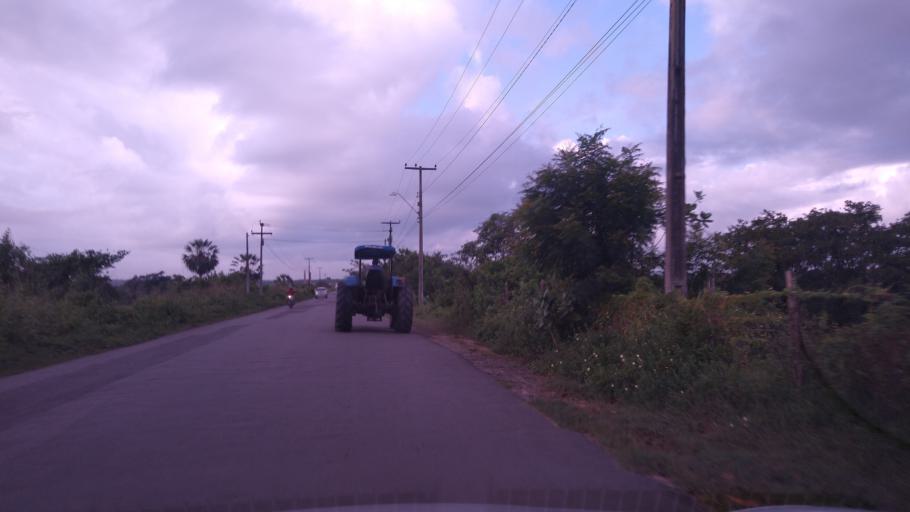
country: BR
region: Ceara
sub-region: Chorozinho
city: Chorozinho
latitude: -4.3049
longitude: -38.4979
